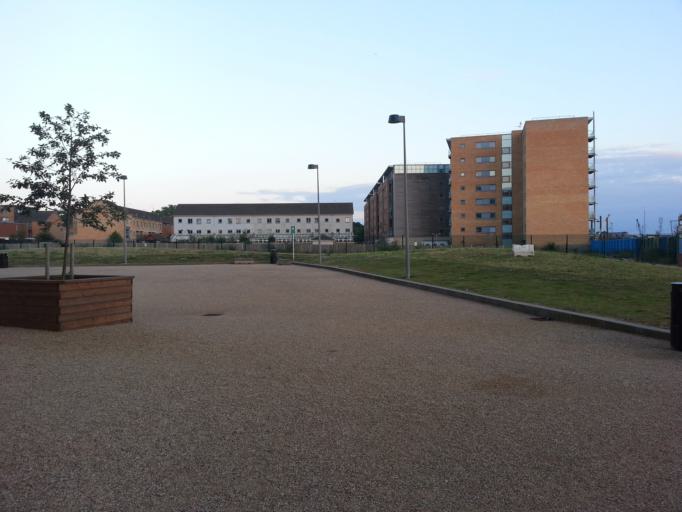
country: GB
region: England
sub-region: Suffolk
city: Ipswich
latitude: 52.0504
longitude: 1.1636
